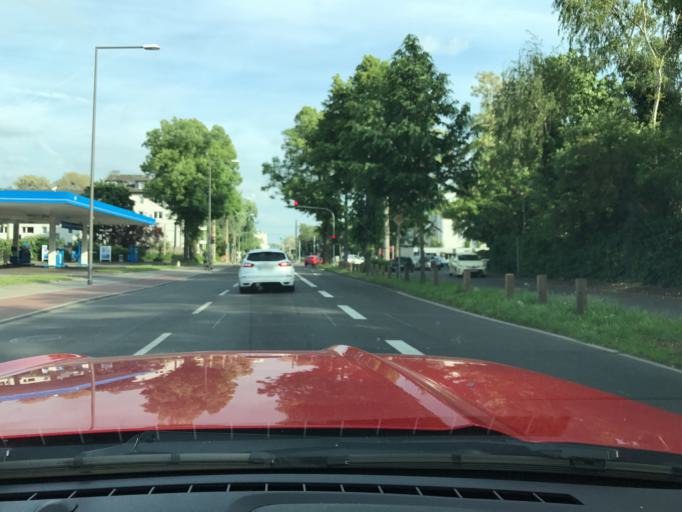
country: DE
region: North Rhine-Westphalia
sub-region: Regierungsbezirk Koln
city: Bilderstoeckchen
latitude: 50.9934
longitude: 6.9399
